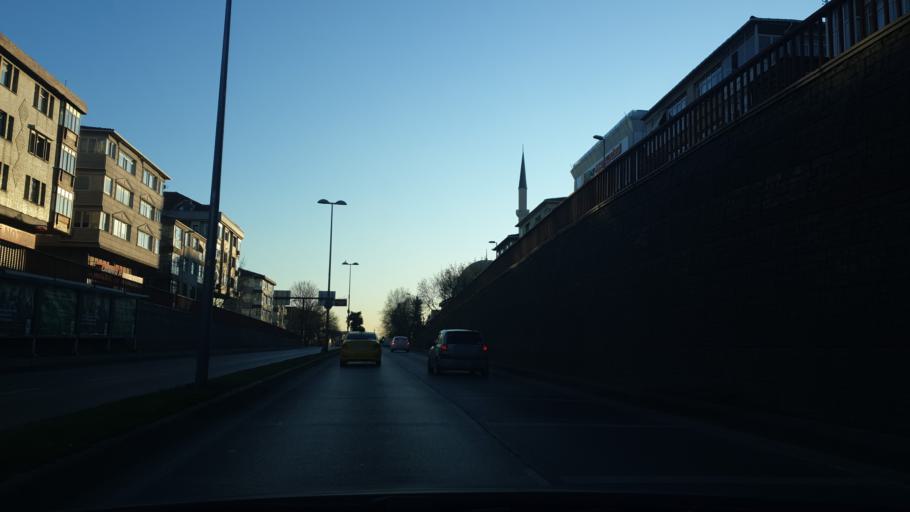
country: TR
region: Istanbul
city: Bahcelievler
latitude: 41.0059
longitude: 28.8699
